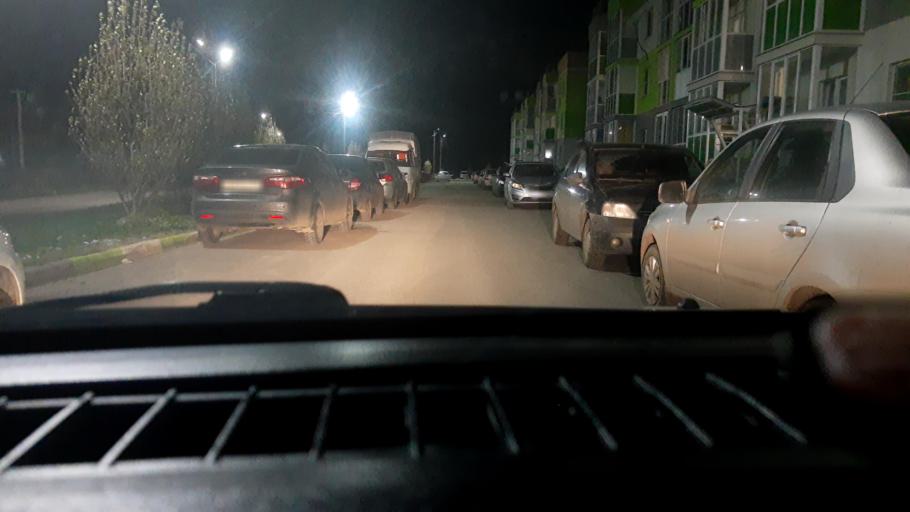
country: RU
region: Nizjnij Novgorod
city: Burevestnik
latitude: 56.1936
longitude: 43.8926
